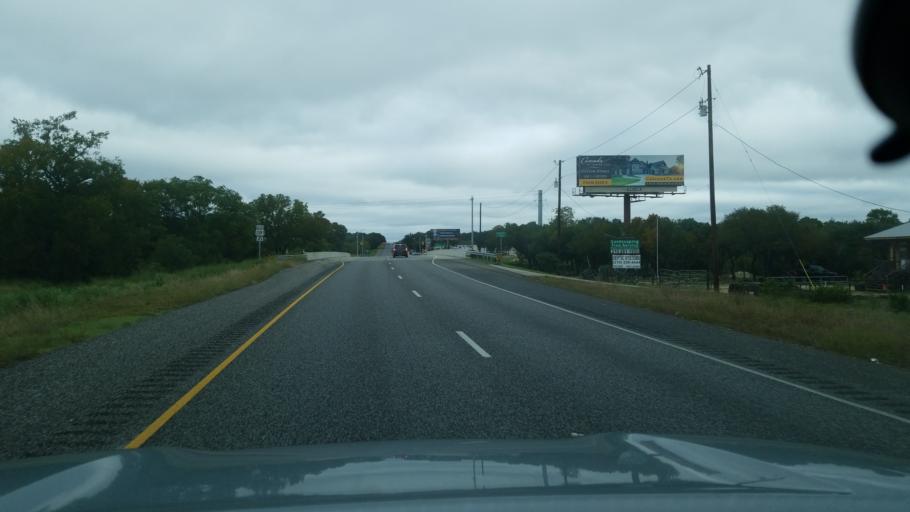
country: US
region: Texas
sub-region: Comal County
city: Bulverde
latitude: 29.8729
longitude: -98.4093
